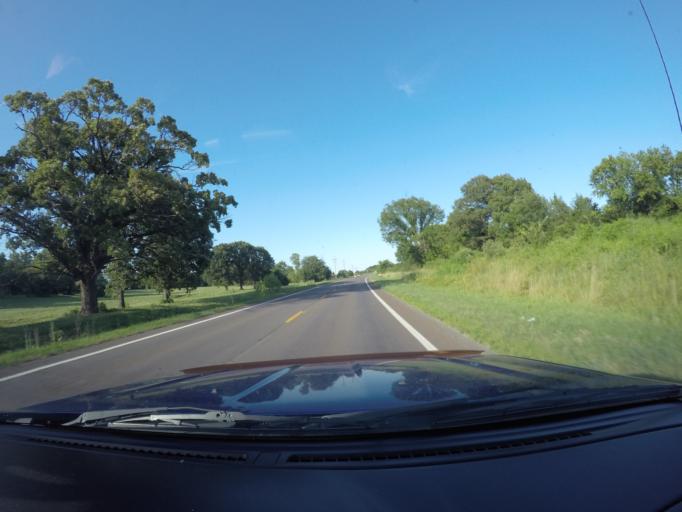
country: US
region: Kansas
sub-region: Douglas County
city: Lawrence
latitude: 39.0075
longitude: -95.1836
